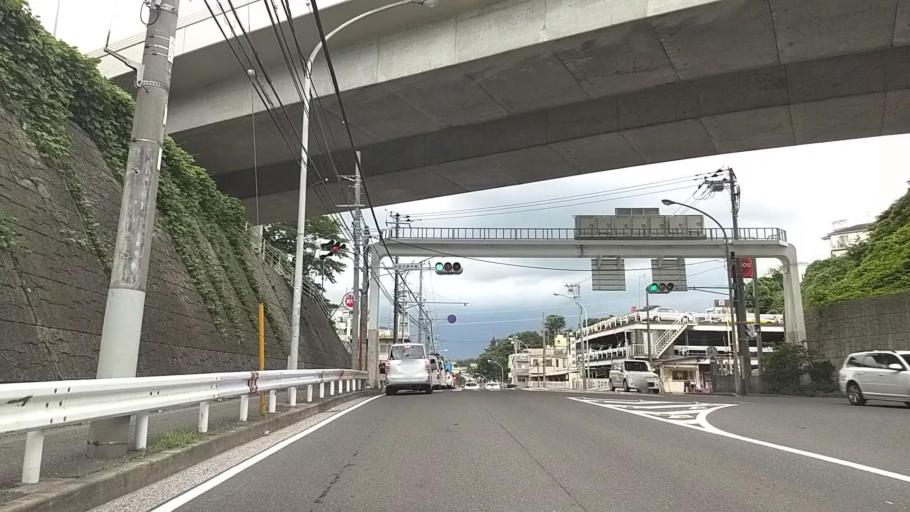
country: JP
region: Kanagawa
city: Yokohama
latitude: 35.4399
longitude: 139.5960
